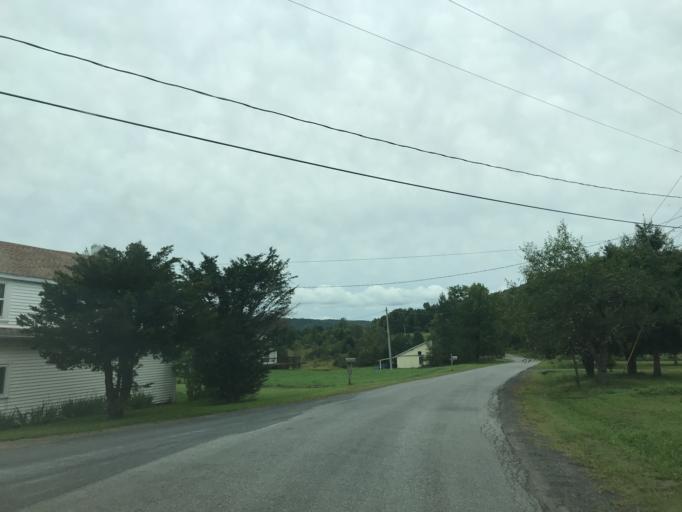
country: US
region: New York
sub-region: Otsego County
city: Worcester
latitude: 42.5651
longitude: -74.6691
